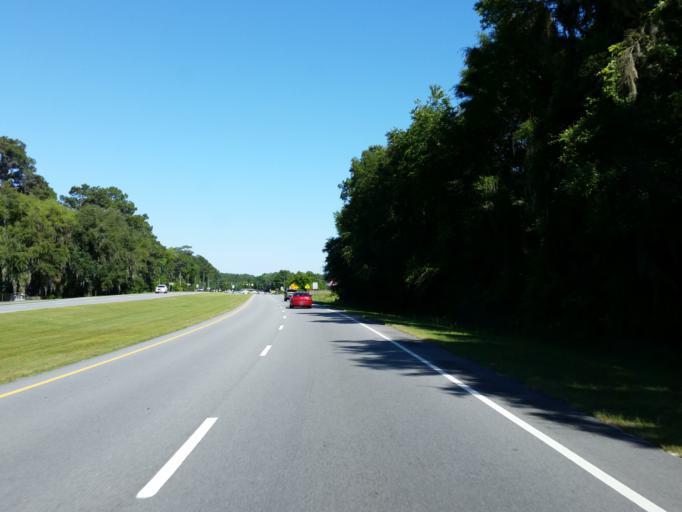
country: US
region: Georgia
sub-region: Lowndes County
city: Valdosta
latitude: 30.6882
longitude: -83.2039
